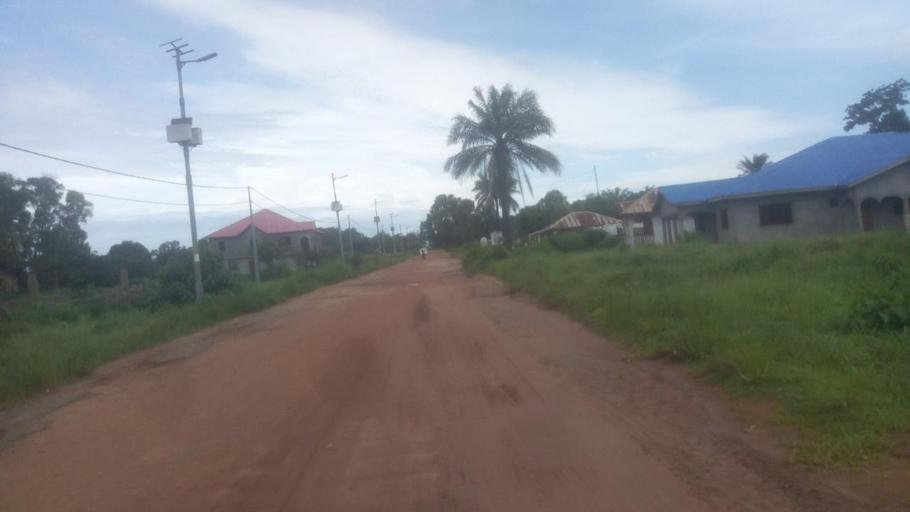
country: SL
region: Northern Province
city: Masoyila
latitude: 8.6019
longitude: -13.1915
